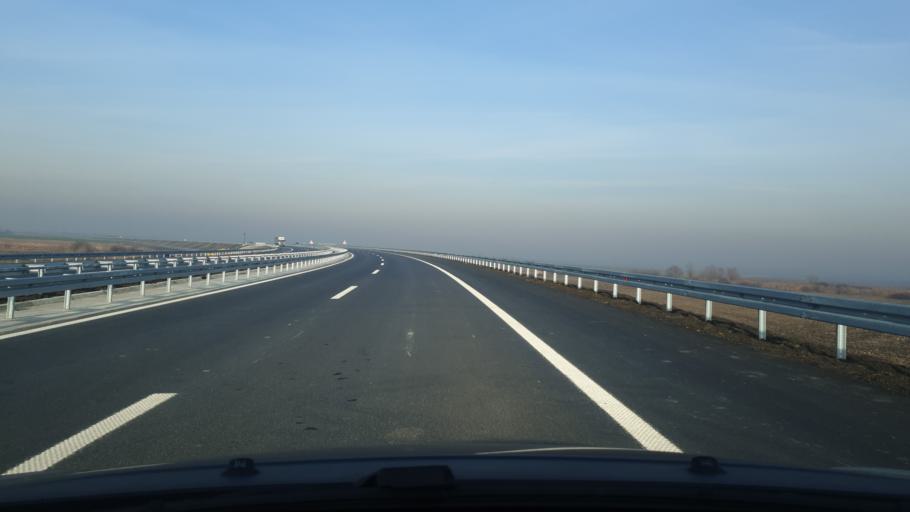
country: RS
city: Baric
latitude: 44.6866
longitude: 20.2666
